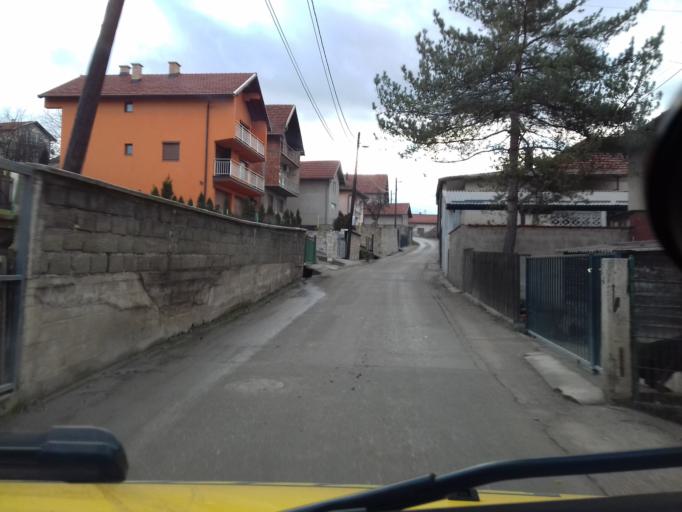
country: BA
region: Federation of Bosnia and Herzegovina
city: Zenica
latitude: 44.2203
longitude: 17.9172
